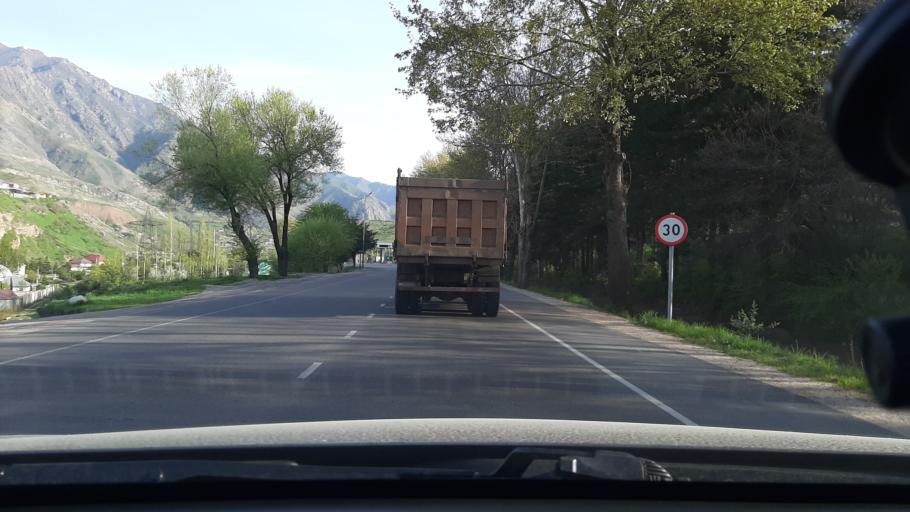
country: TJ
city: Varzob
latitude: 38.6807
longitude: 68.7915
